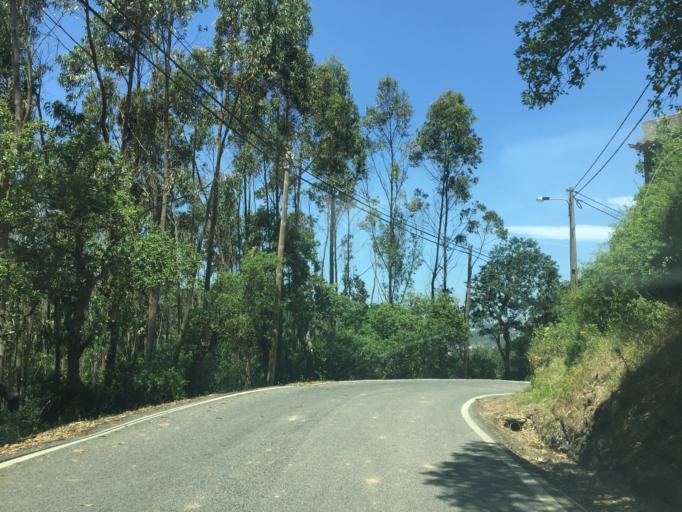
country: PT
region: Lisbon
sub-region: Mafra
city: Venda do Pinheiro
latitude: 38.8886
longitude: -9.2228
